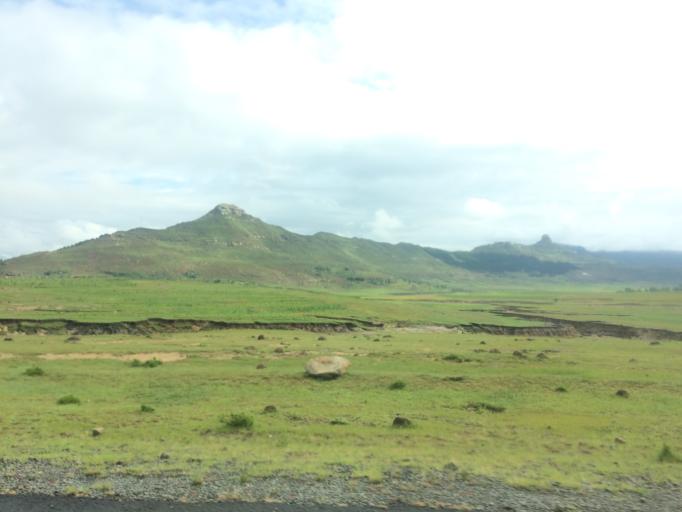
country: LS
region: Mafeteng
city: Mafeteng
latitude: -29.7067
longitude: 27.4654
